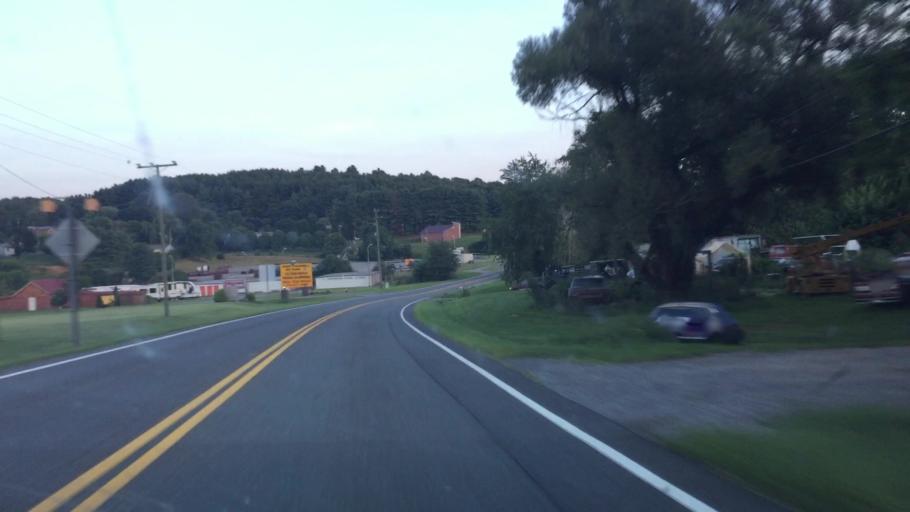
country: US
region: Virginia
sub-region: Wythe County
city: Wytheville
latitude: 36.9411
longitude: -80.9438
